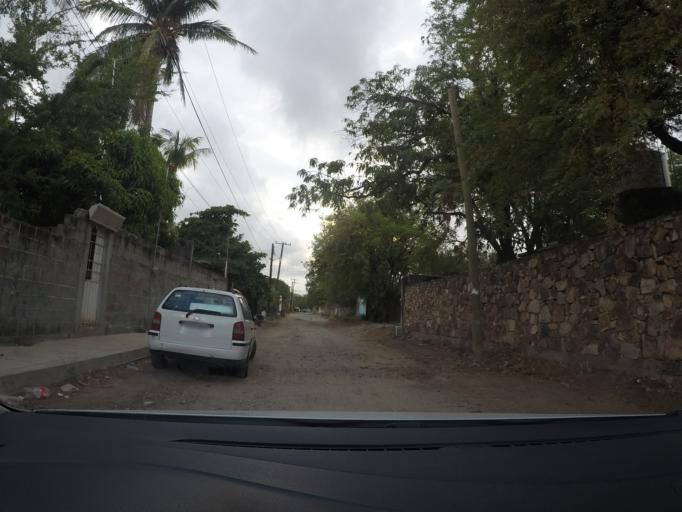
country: MX
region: Oaxaca
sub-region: Salina Cruz
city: Salina Cruz
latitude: 16.2095
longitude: -95.1972
